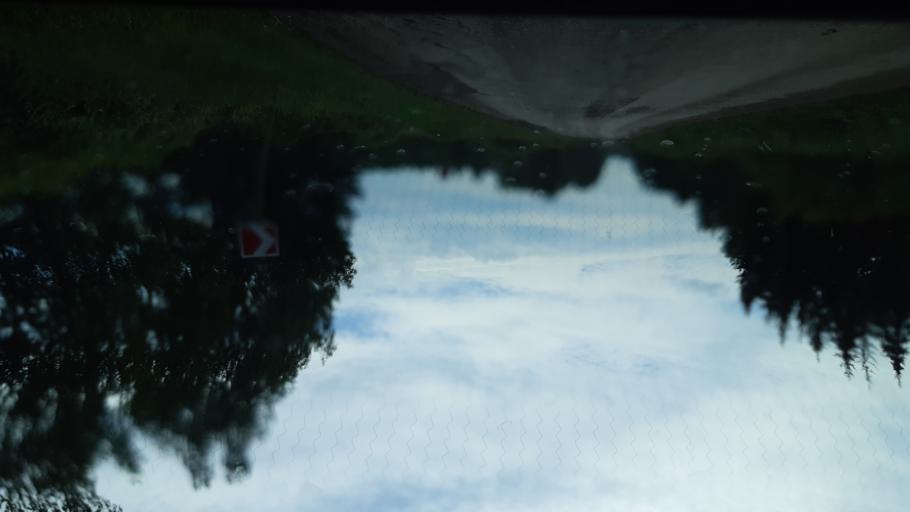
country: RU
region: Moskovskaya
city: Vereya
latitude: 55.3162
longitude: 36.1262
